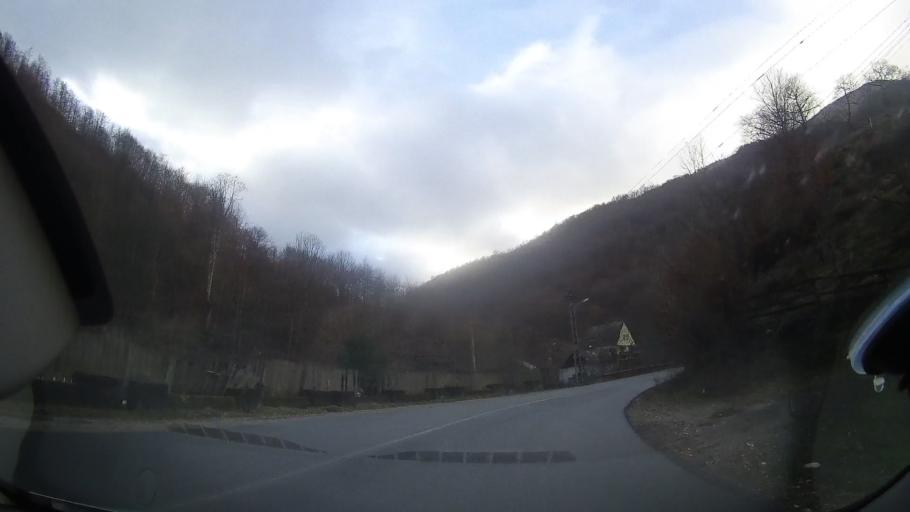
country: RO
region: Cluj
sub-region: Comuna Maguri-Racatau
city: Maguri-Racatau
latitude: 46.6770
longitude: 23.2598
